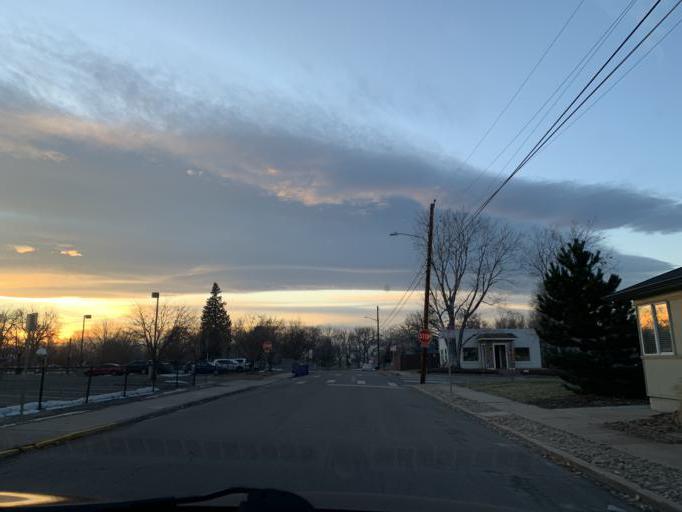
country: US
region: Colorado
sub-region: Adams County
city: Berkley
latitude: 39.7821
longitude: -105.0424
